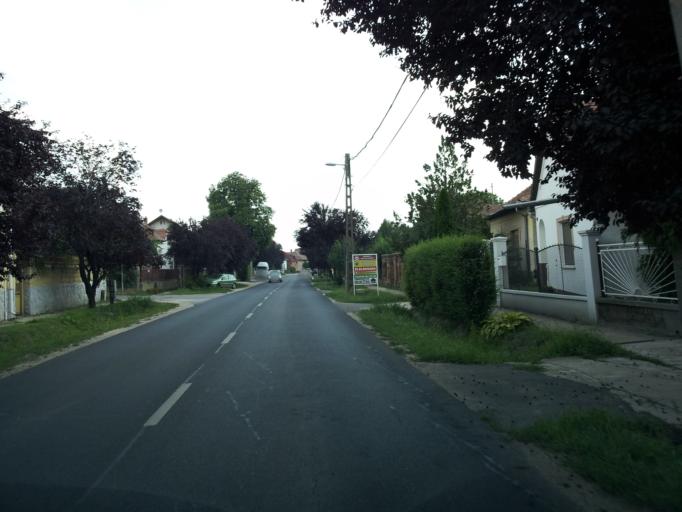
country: HU
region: Pest
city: Toekoel
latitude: 47.3289
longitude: 18.9647
